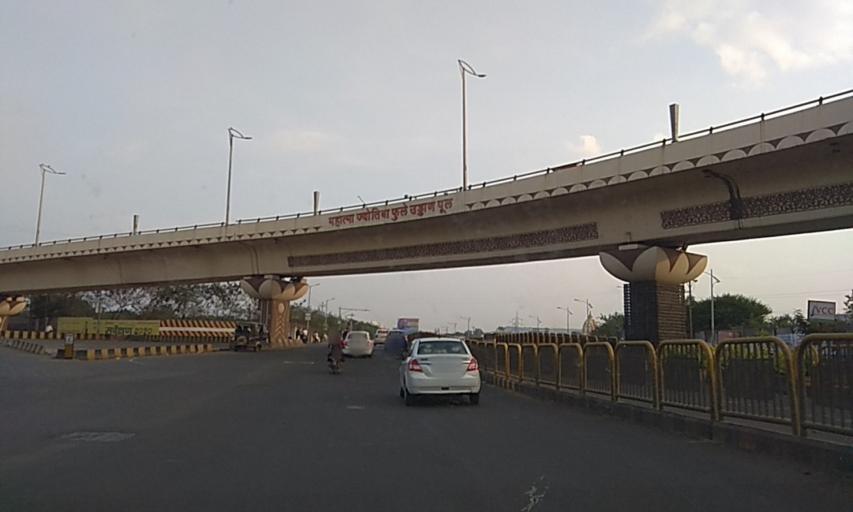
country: IN
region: Maharashtra
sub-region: Pune Division
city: Khadki
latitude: 18.5740
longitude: 73.8062
